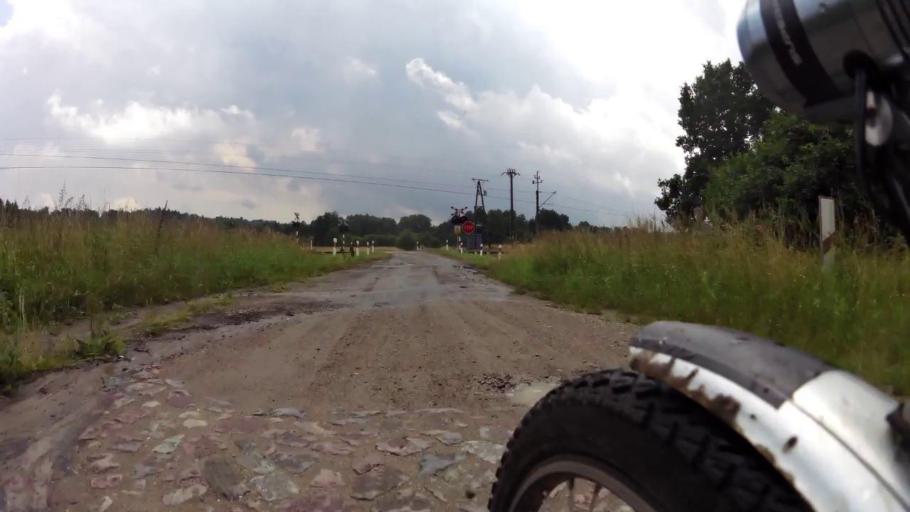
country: PL
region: West Pomeranian Voivodeship
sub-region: Powiat lobeski
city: Lobez
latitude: 53.7283
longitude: 15.6771
